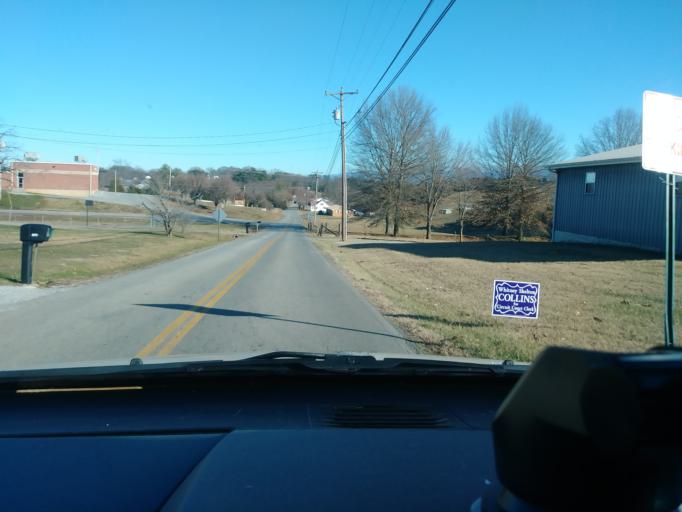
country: US
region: Tennessee
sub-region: Greene County
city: Greeneville
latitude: 36.1127
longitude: -82.8780
